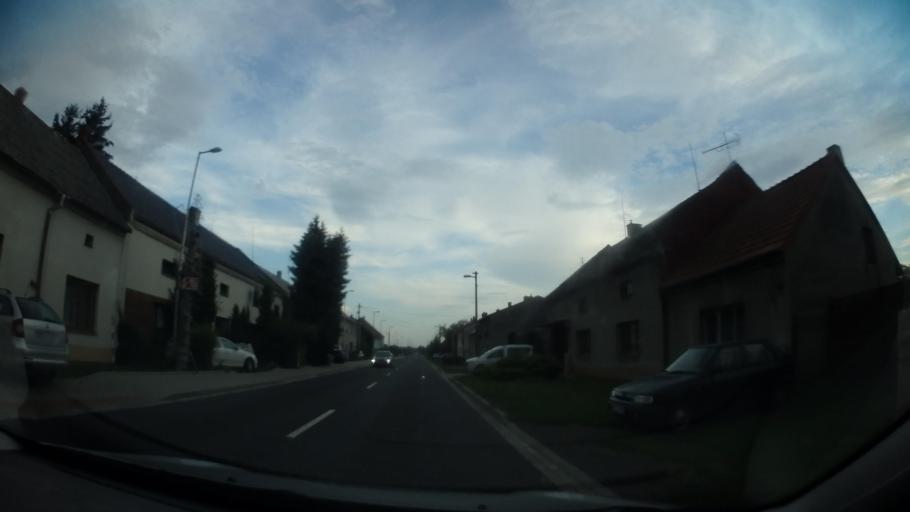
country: CZ
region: Olomoucky
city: Troubky
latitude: 49.4296
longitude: 17.3397
